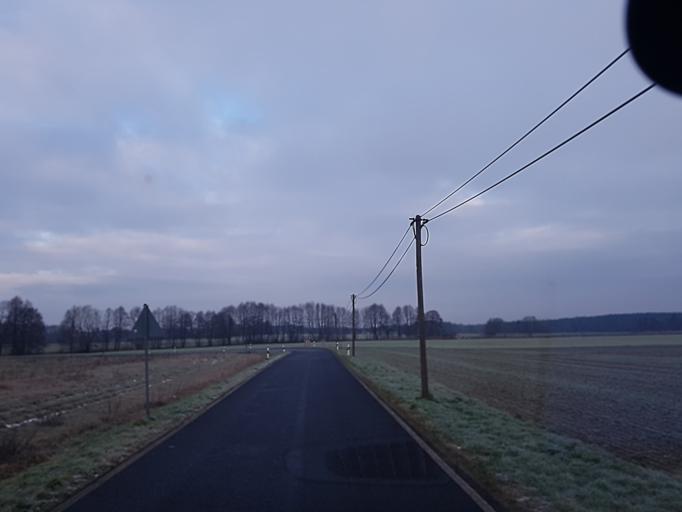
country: DE
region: Brandenburg
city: Crinitz
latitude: 51.7288
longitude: 13.8372
